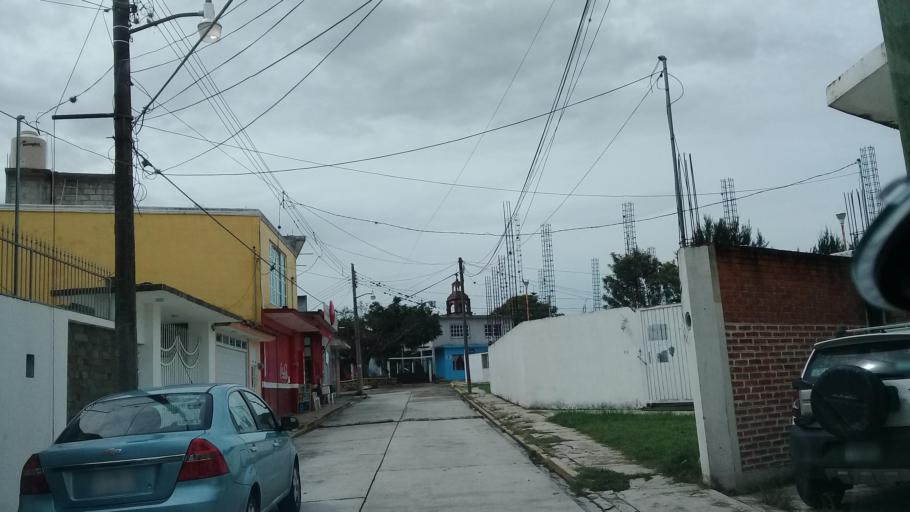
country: MX
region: Veracruz
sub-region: Emiliano Zapata
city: Dos Rios
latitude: 19.4811
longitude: -96.7983
